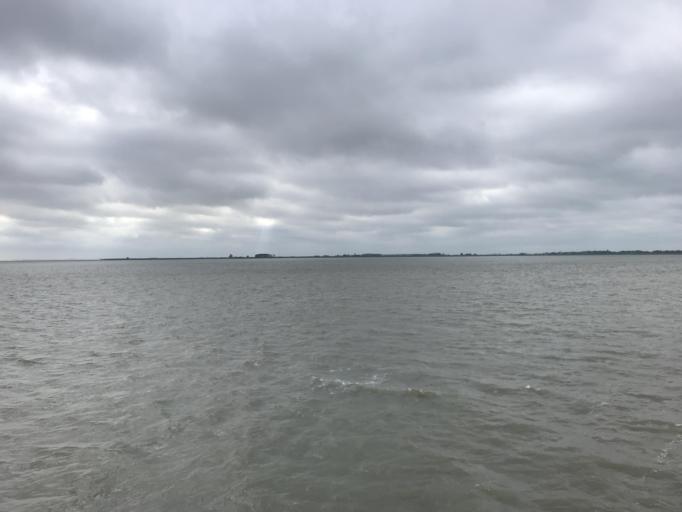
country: NL
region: Groningen
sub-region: Gemeente Delfzijl
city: Delfzijl
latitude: 53.3246
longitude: 7.0603
